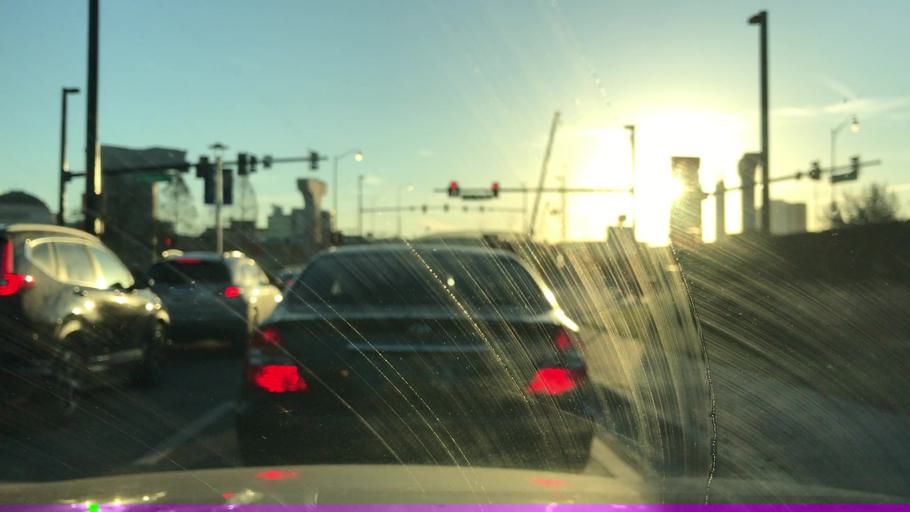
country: US
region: Florida
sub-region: Orange County
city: Orlando
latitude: 28.5366
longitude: -81.3853
